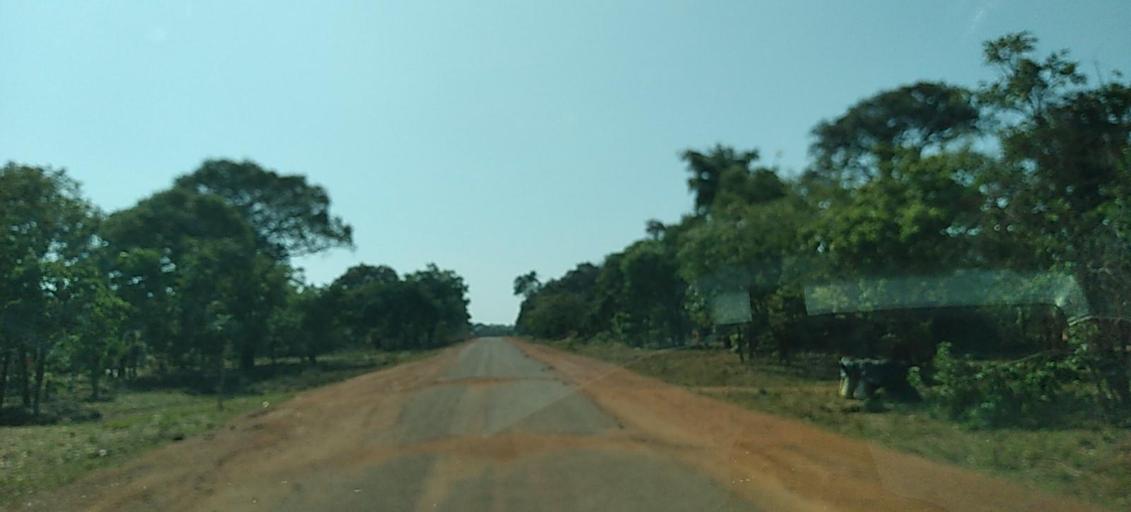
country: ZM
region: North-Western
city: Mwinilunga
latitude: -11.8909
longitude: 25.2630
